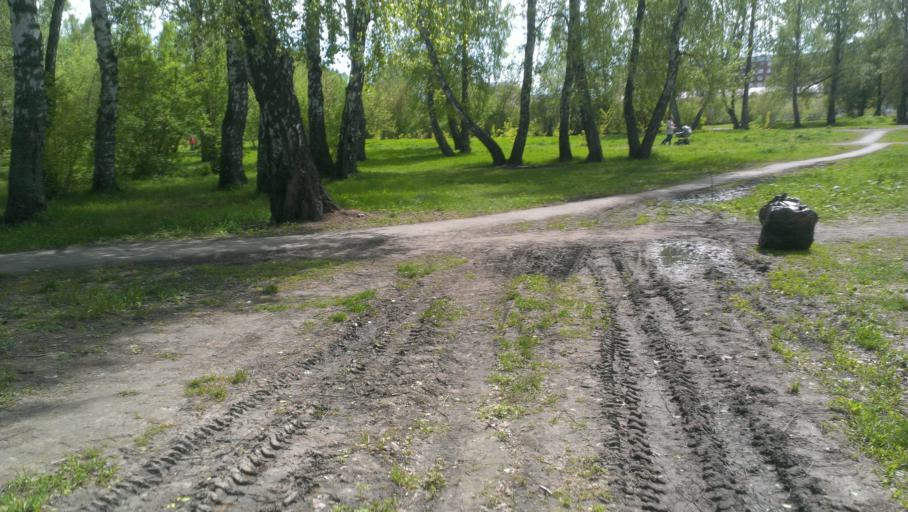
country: RU
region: Altai Krai
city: Novosilikatnyy
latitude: 53.3616
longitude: 83.6677
